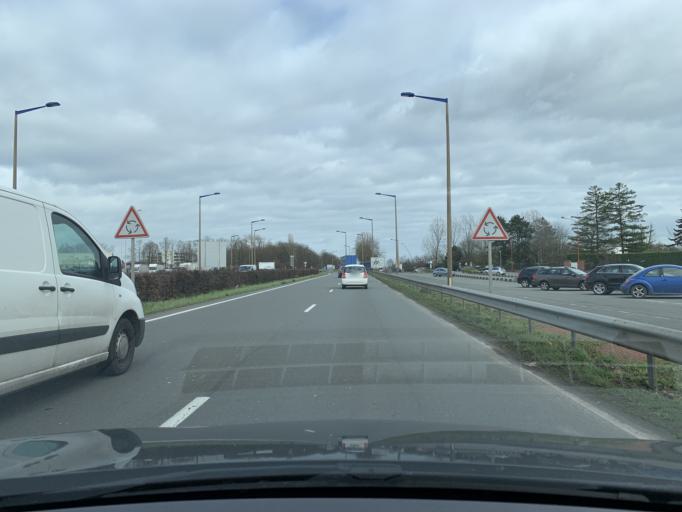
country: FR
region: Nord-Pas-de-Calais
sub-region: Departement du Nord
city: Dechy
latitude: 50.3403
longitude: 3.0999
